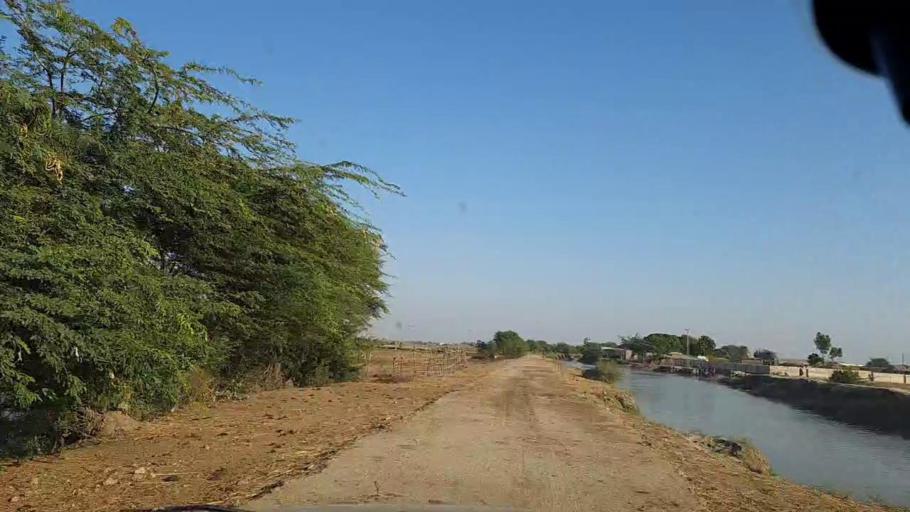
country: PK
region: Sindh
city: Chuhar Jamali
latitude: 24.5637
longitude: 68.0660
